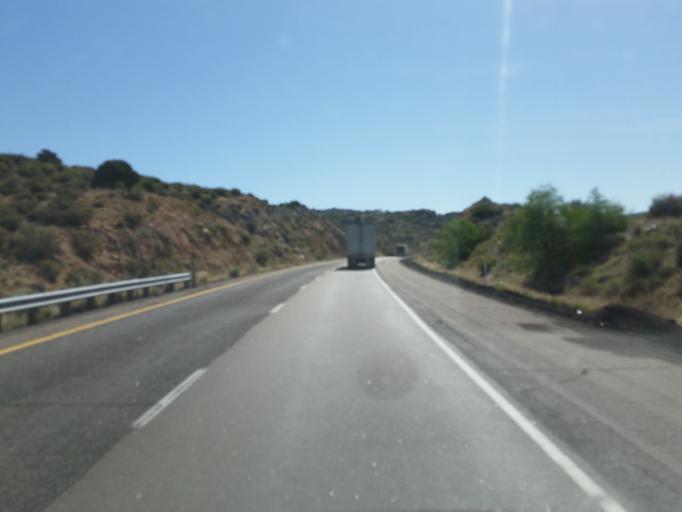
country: US
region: Arizona
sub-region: Mohave County
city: Peach Springs
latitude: 35.1768
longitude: -113.4901
